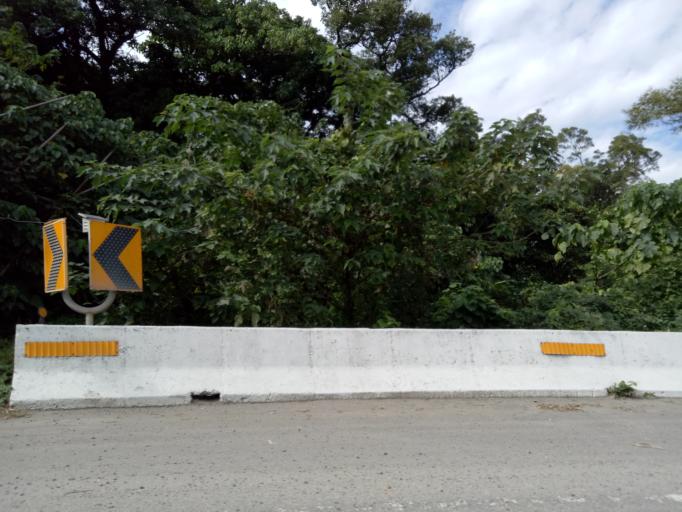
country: TW
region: Taiwan
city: Daxi
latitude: 24.9027
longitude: 121.2918
